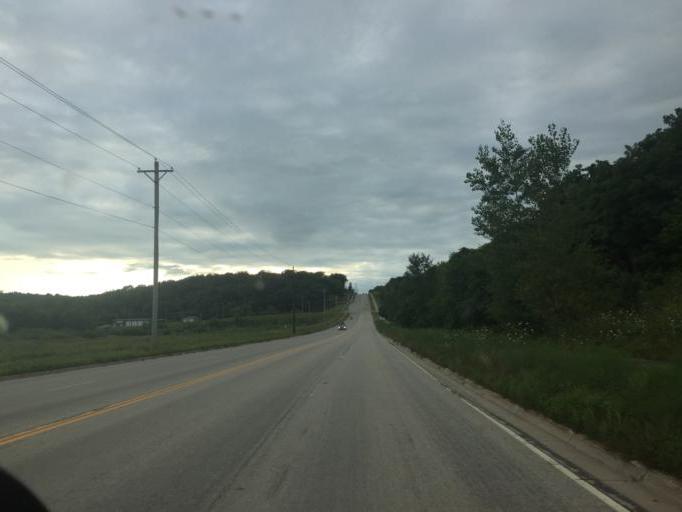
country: US
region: Minnesota
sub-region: Olmsted County
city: Rochester
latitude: 43.9640
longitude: -92.4737
